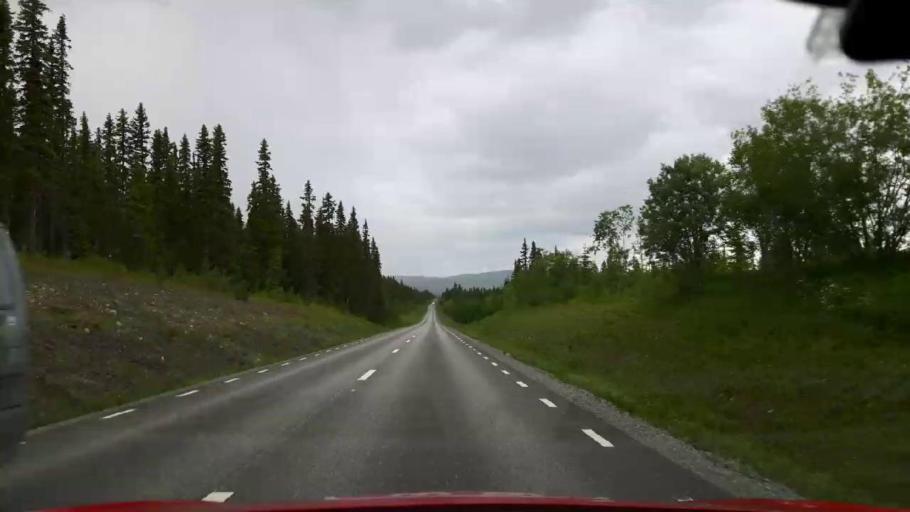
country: SE
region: Jaemtland
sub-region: Krokoms Kommun
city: Krokom
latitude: 63.7065
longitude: 14.3119
